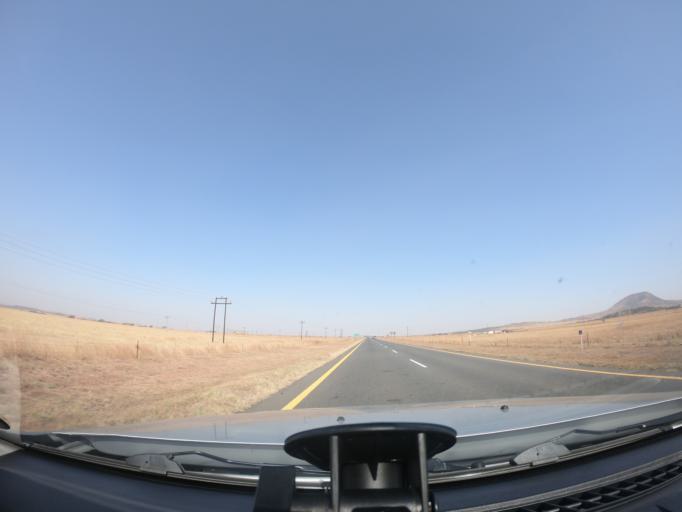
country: ZA
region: KwaZulu-Natal
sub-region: uThukela District Municipality
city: Ekuvukeni
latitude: -28.3755
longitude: 29.9472
